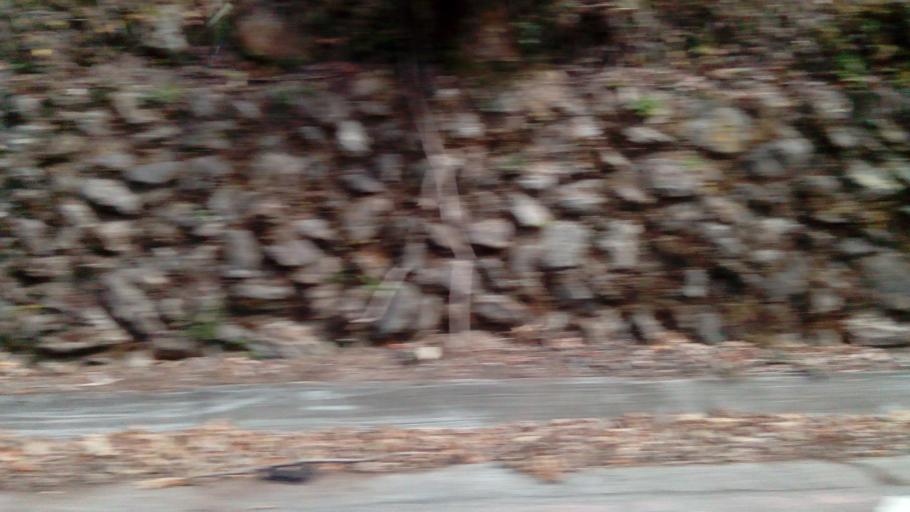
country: TW
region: Taiwan
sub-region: Hualien
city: Hualian
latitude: 24.3572
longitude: 121.3255
